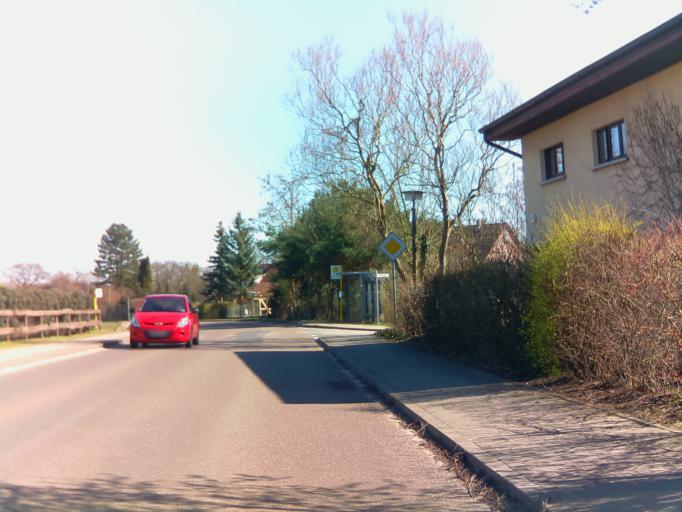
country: DE
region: Brandenburg
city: Werder
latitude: 52.4342
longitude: 12.9342
